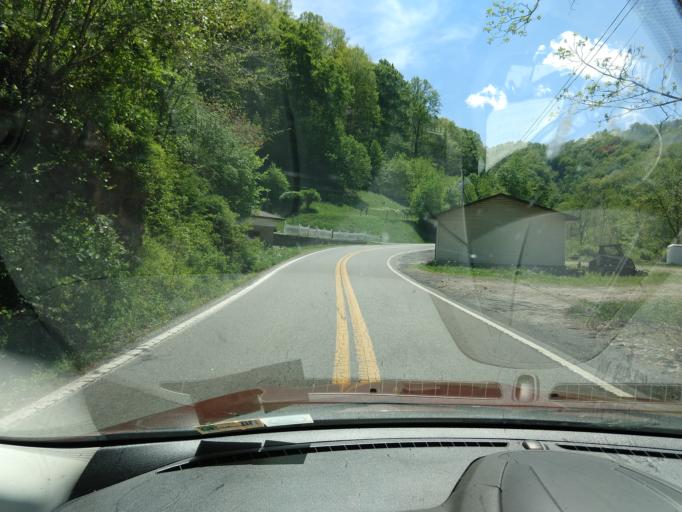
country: US
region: West Virginia
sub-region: McDowell County
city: Welch
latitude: 37.3169
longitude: -81.6953
